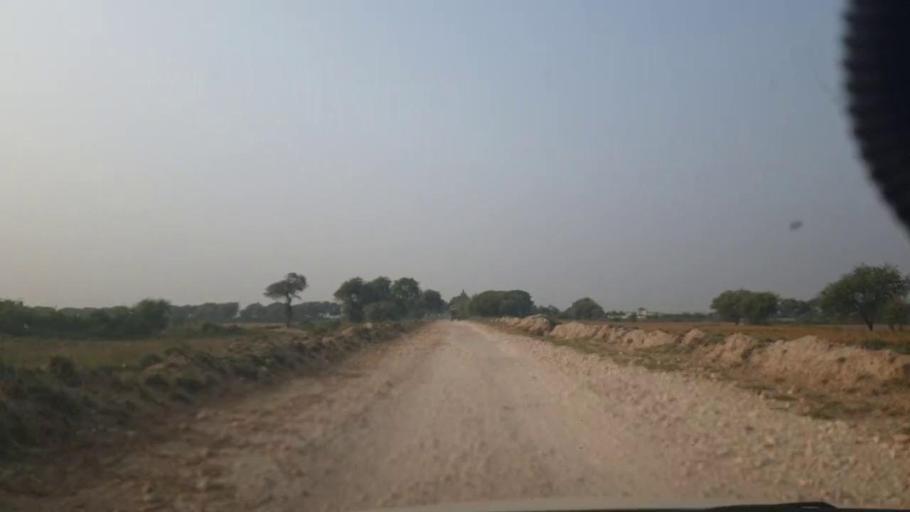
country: PK
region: Sindh
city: Bulri
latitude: 24.8021
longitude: 68.4132
